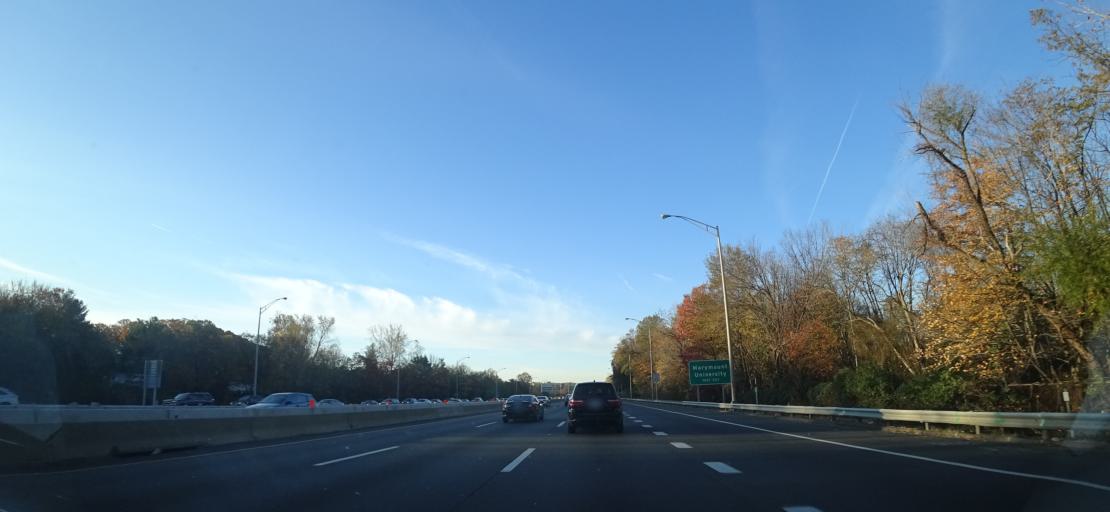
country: US
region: Virginia
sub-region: Arlington County
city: Arlington
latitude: 38.8548
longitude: -77.0736
